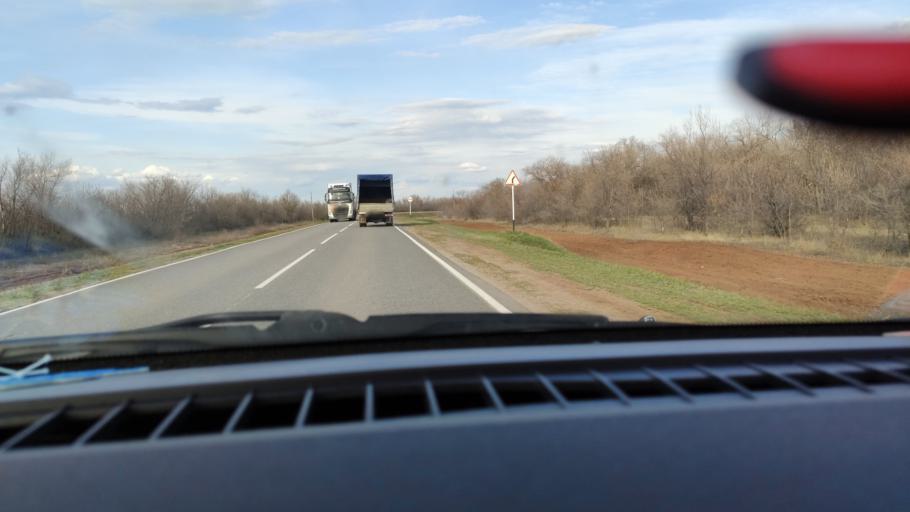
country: RU
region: Saratov
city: Privolzhskiy
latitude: 51.2896
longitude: 45.9798
